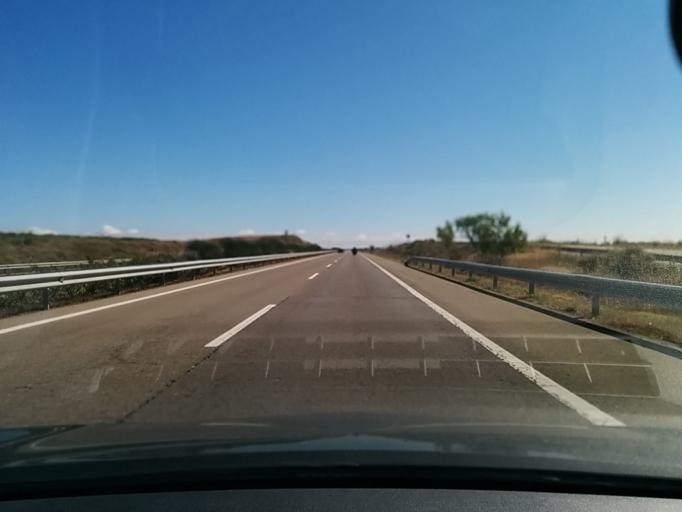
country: ES
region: Aragon
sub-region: Provincia de Huesca
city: Almudebar
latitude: 42.0110
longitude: -0.6268
